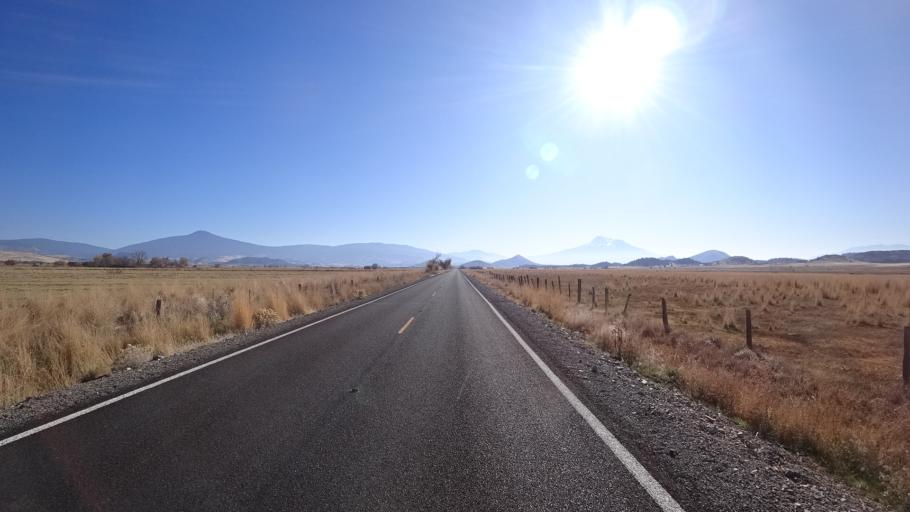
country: US
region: California
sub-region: Siskiyou County
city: Montague
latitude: 41.7158
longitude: -122.4446
